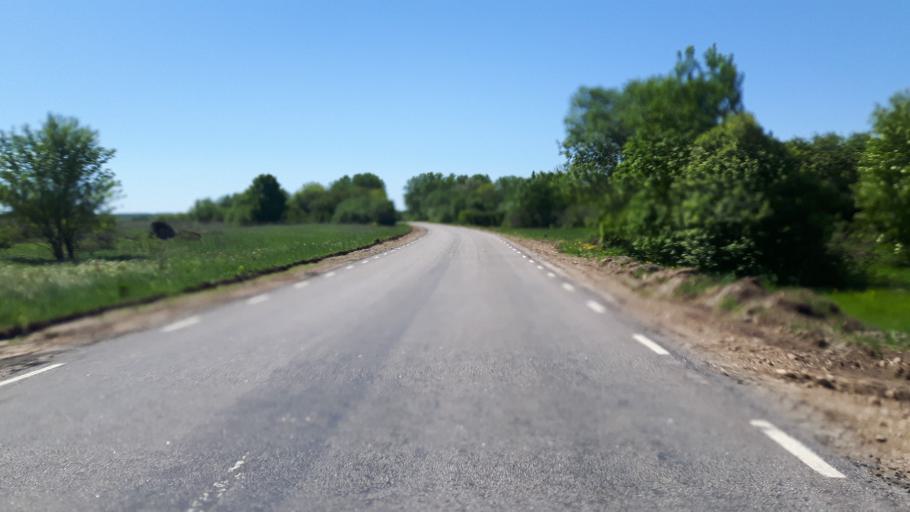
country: EE
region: Ida-Virumaa
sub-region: Narva-Joesuu linn
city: Narva-Joesuu
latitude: 59.3942
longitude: 27.9251
